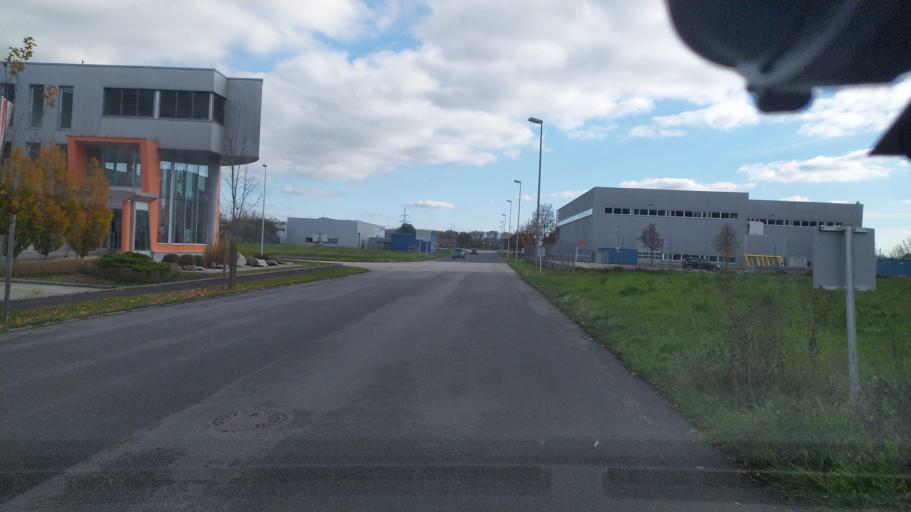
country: AT
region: Upper Austria
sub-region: Politischer Bezirk Urfahr-Umgebung
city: Steyregg
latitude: 48.2501
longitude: 14.3797
